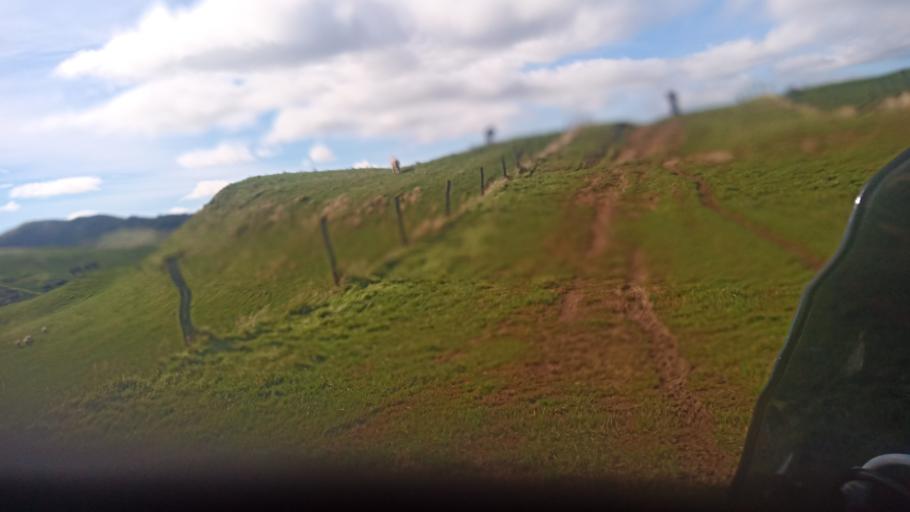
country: NZ
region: Gisborne
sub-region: Gisborne District
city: Gisborne
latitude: -38.4860
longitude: 177.5434
